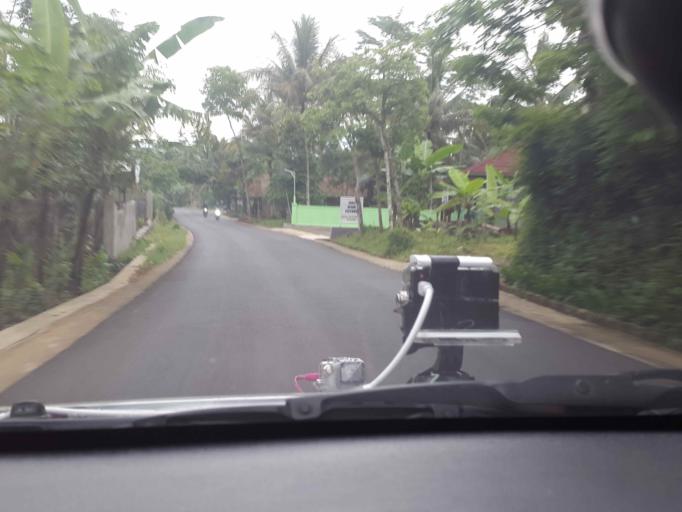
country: ID
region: Central Java
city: Banyumas
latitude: -7.5528
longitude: 109.3150
